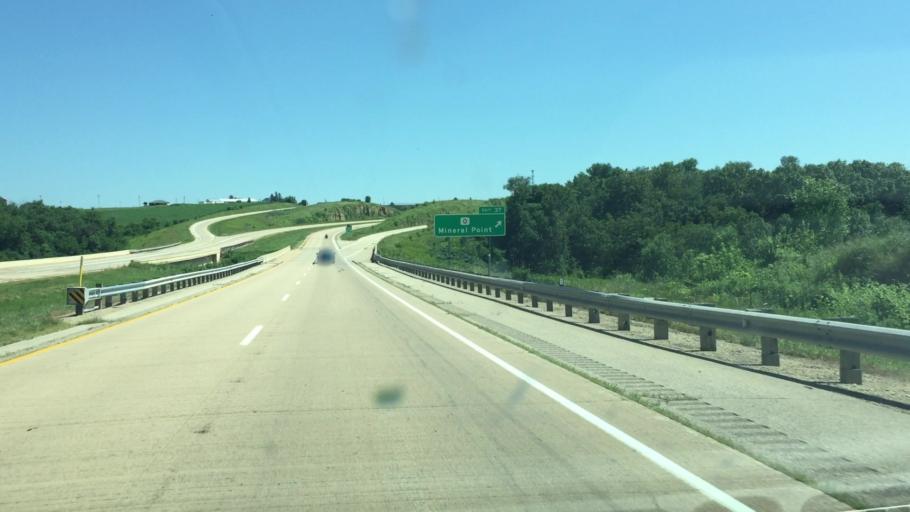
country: US
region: Wisconsin
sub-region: Iowa County
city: Mineral Point
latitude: 42.8545
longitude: -90.2016
